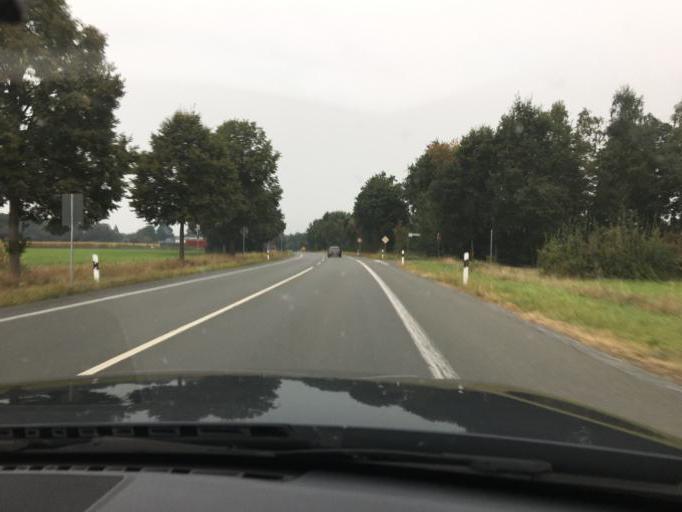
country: DE
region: North Rhine-Westphalia
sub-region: Regierungsbezirk Munster
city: Ladbergen
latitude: 52.1081
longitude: 7.7038
